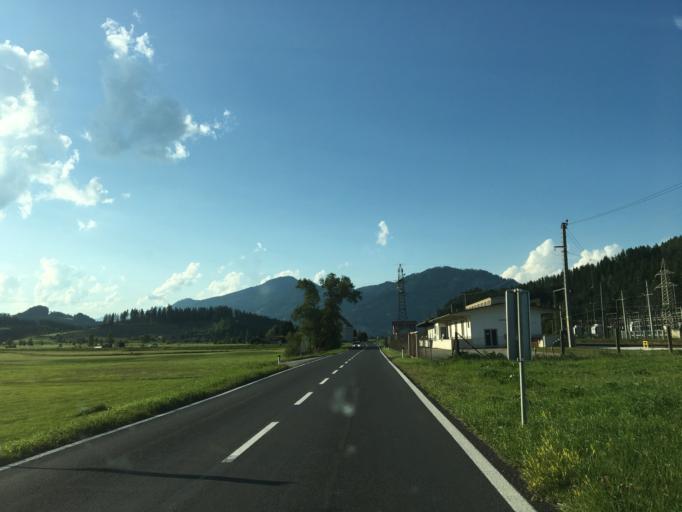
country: AT
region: Styria
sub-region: Politischer Bezirk Murau
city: Mariahof
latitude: 47.1035
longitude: 14.3743
